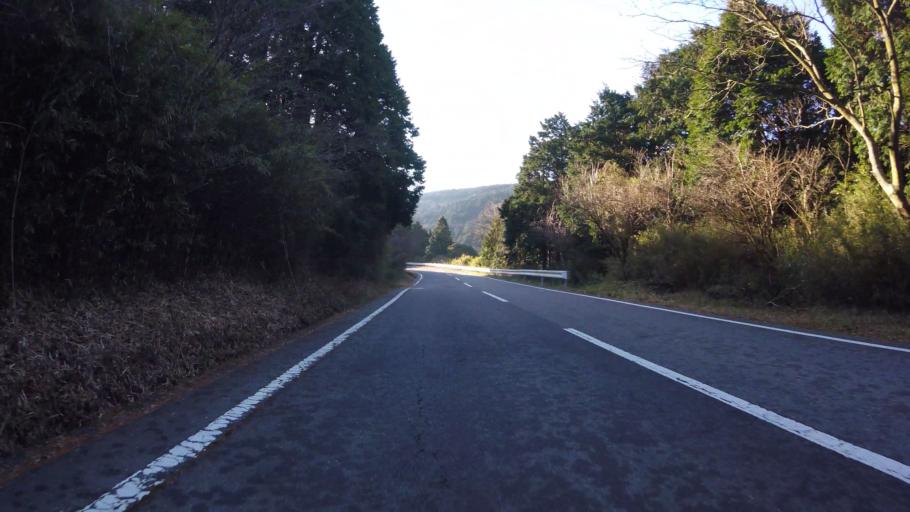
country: JP
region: Kanagawa
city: Yugawara
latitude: 35.1241
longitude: 139.0354
